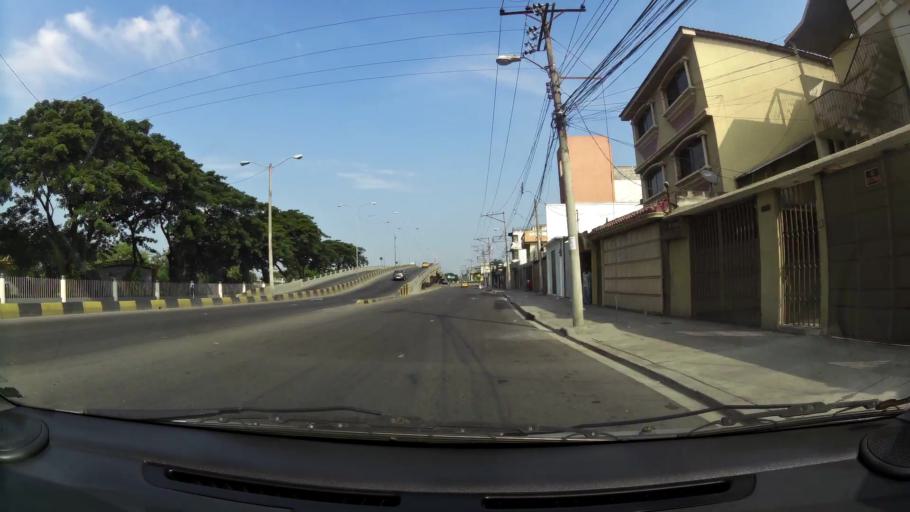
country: EC
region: Guayas
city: Guayaquil
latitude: -2.1885
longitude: -79.9109
